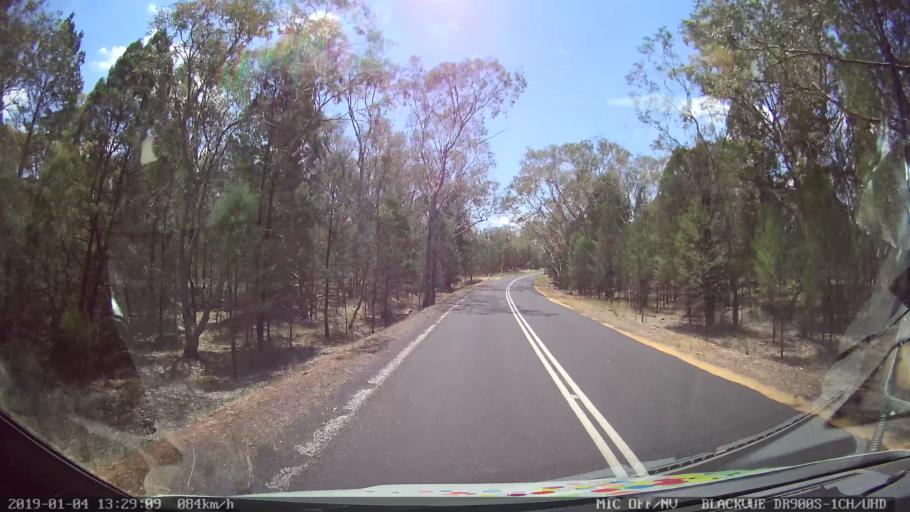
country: AU
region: New South Wales
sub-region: Parkes
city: Peak Hill
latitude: -32.6501
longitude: 148.5508
